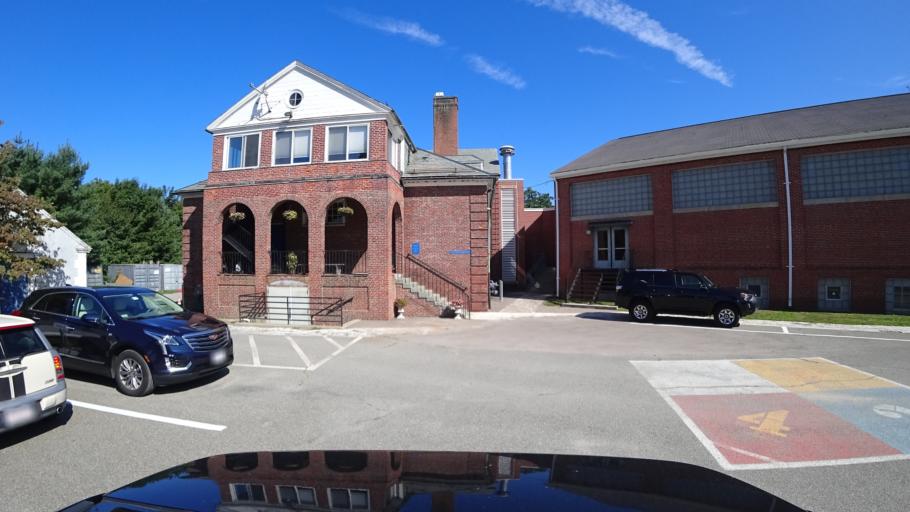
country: US
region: Massachusetts
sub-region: Norfolk County
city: Dedham
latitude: 42.2586
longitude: -71.1880
